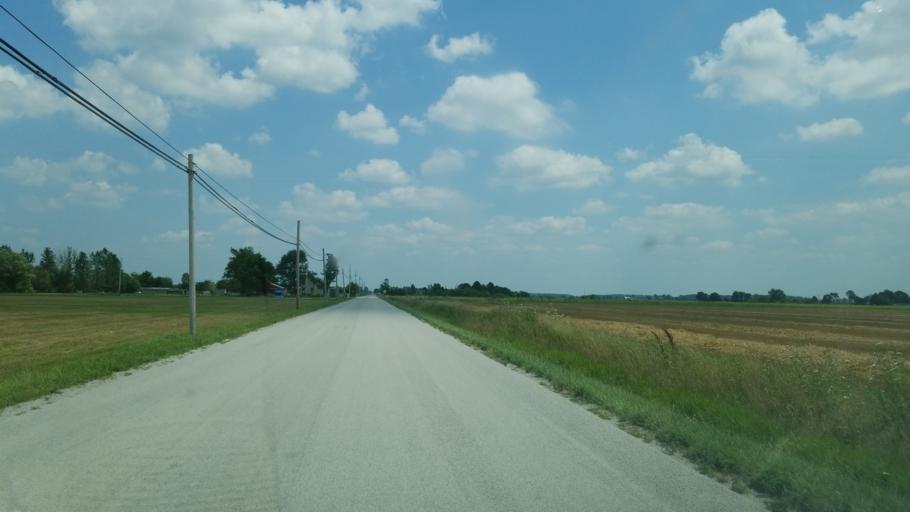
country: US
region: Ohio
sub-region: Wood County
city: North Baltimore
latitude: 41.2402
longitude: -83.6090
